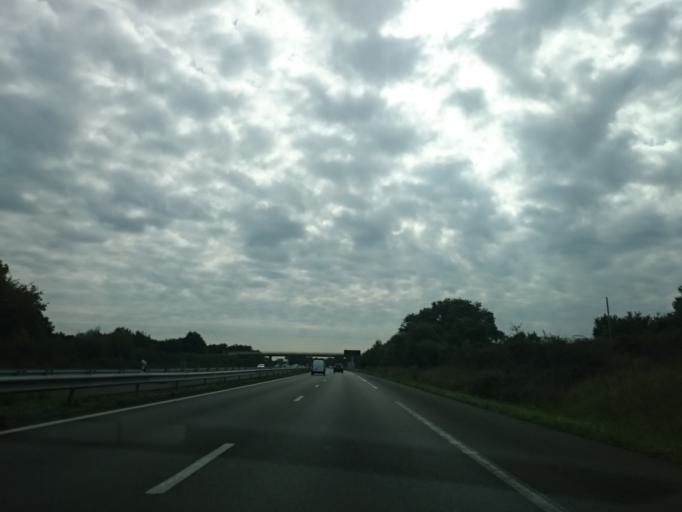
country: FR
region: Pays de la Loire
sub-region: Departement de la Loire-Atlantique
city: Sautron
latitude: 47.2639
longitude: -1.7060
